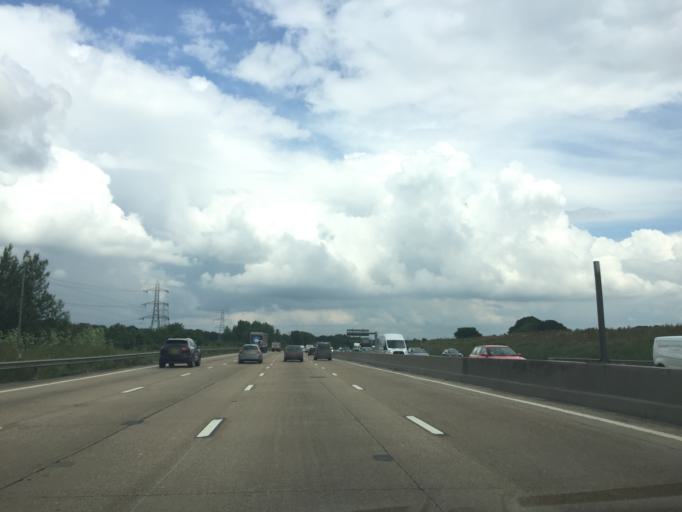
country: GB
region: England
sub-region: Greater London
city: Hadley Wood
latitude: 51.6864
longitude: -0.1433
